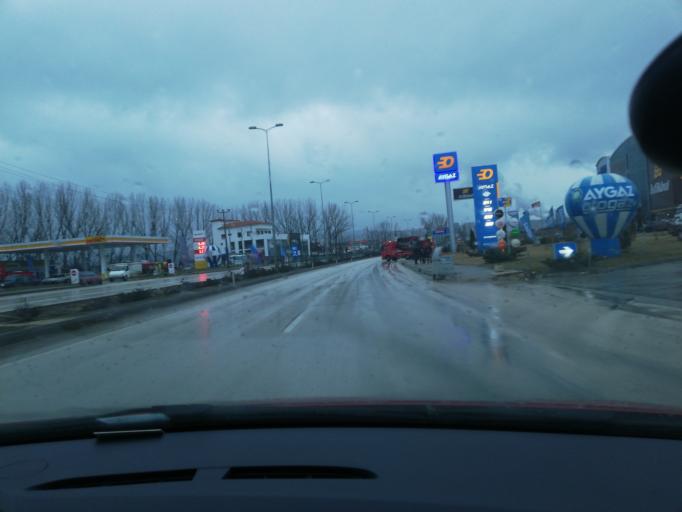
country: TR
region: Kastamonu
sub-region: Cide
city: Kastamonu
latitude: 41.4236
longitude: 33.8020
